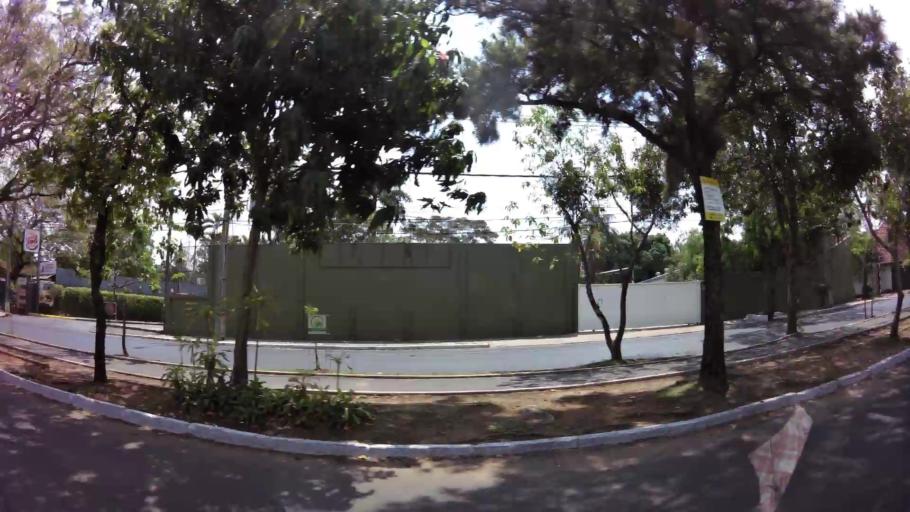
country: PY
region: Central
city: Lambare
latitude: -25.2996
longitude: -57.5707
